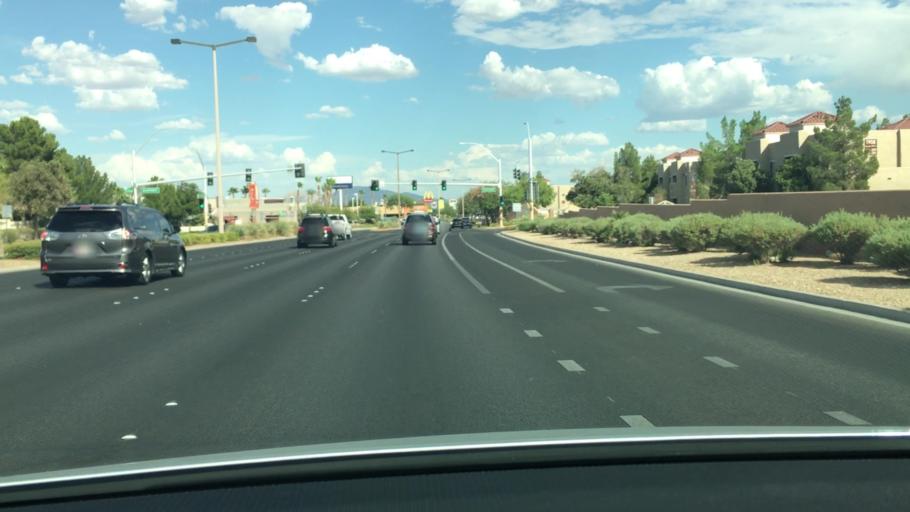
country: US
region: Nevada
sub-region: Clark County
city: Spring Valley
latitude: 36.1970
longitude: -115.2659
